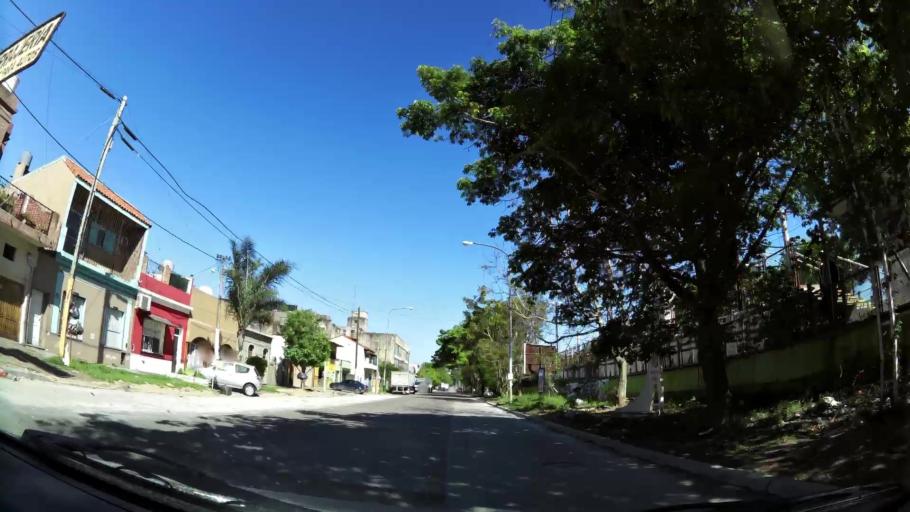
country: AR
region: Buenos Aires
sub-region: Partido de Quilmes
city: Quilmes
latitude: -34.7048
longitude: -58.2916
